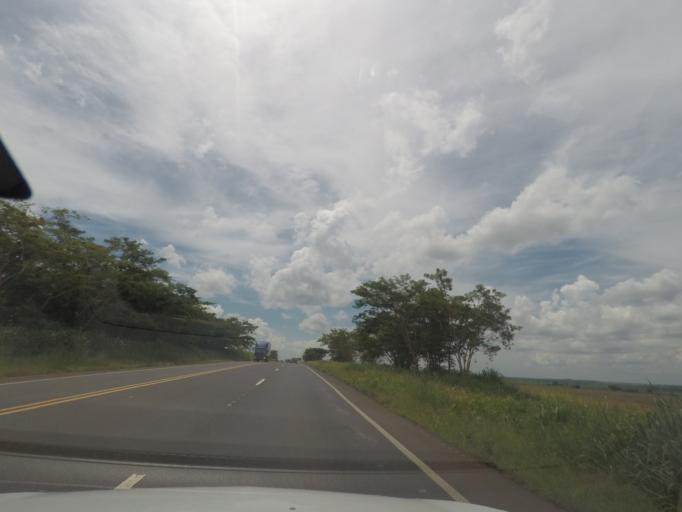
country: BR
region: Sao Paulo
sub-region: Barretos
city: Barretos
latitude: -20.3964
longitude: -48.6379
